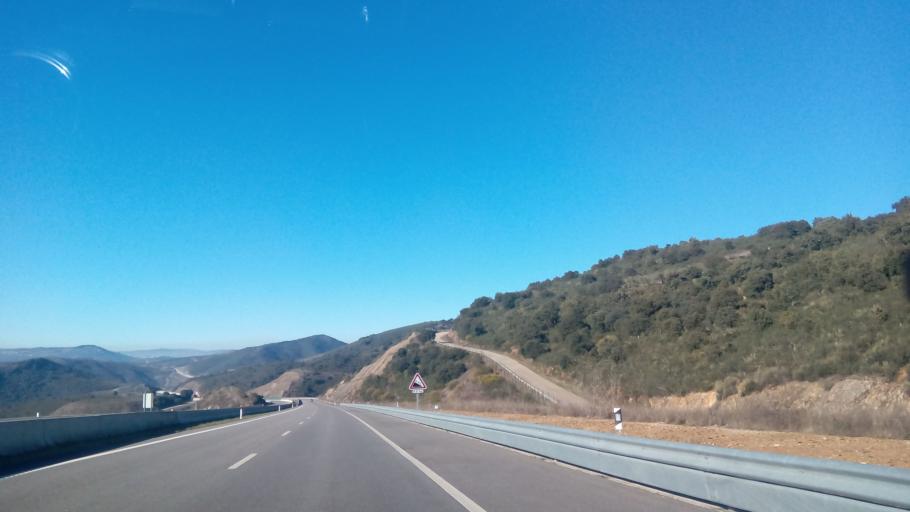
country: PT
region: Braganca
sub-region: Braganca Municipality
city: Braganca
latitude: 41.7643
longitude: -6.6527
